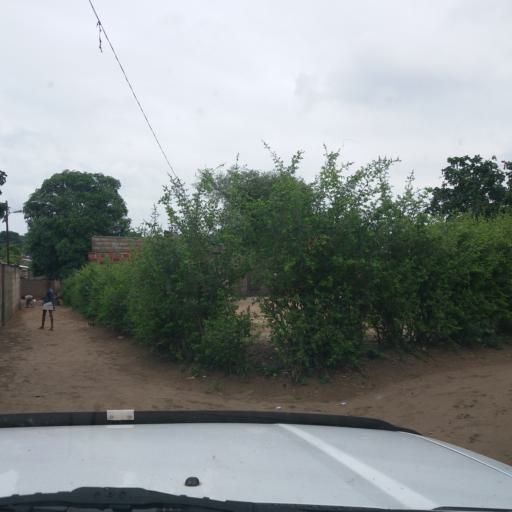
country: MZ
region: Maputo City
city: Maputo
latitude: -25.9040
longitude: 32.5934
